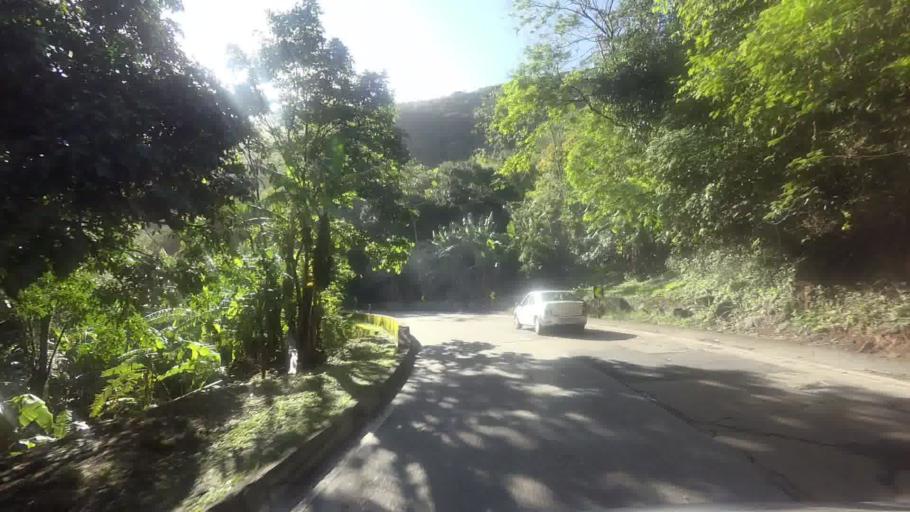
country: BR
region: Rio de Janeiro
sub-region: Petropolis
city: Petropolis
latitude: -22.5685
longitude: -43.2421
